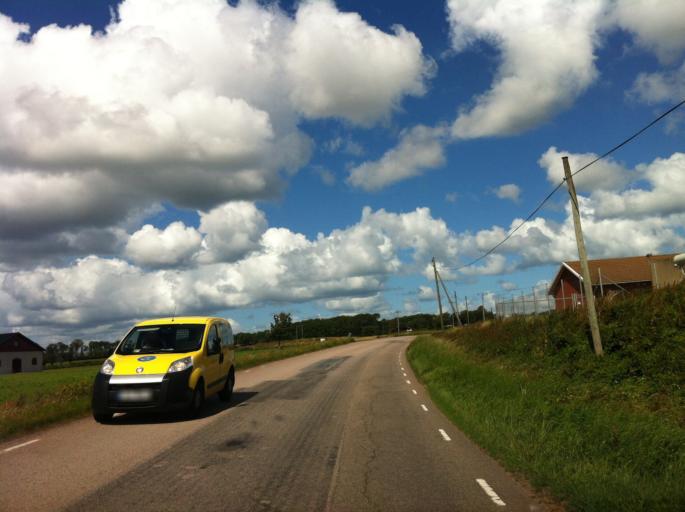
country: SE
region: Skane
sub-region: Angelholms Kommun
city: AEngelholm
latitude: 56.2541
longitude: 12.8780
